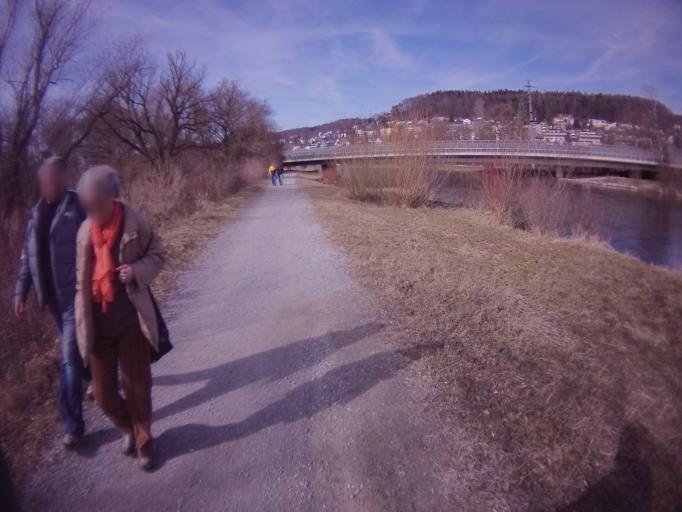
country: CH
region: Zurich
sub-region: Bezirk Dietikon
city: Geroldswil
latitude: 47.4203
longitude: 8.4026
